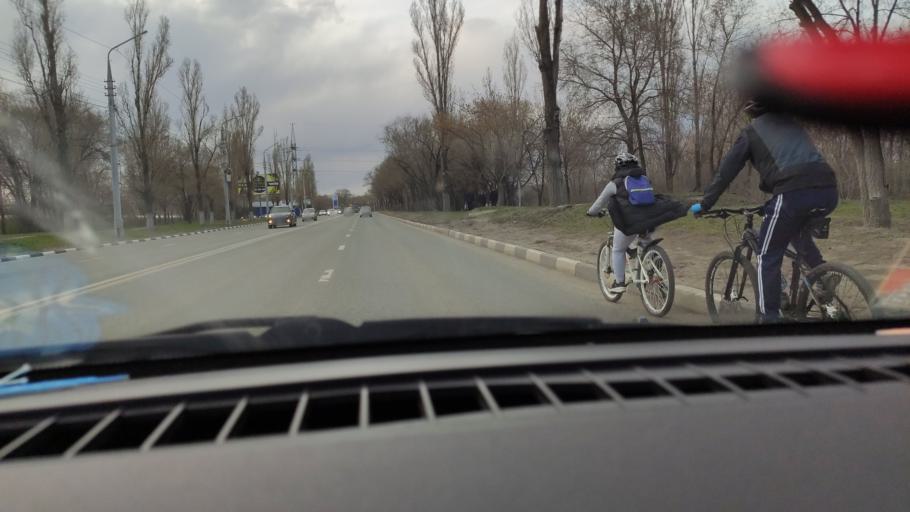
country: RU
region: Saratov
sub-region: Saratovskiy Rayon
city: Saratov
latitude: 51.5788
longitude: 45.9845
